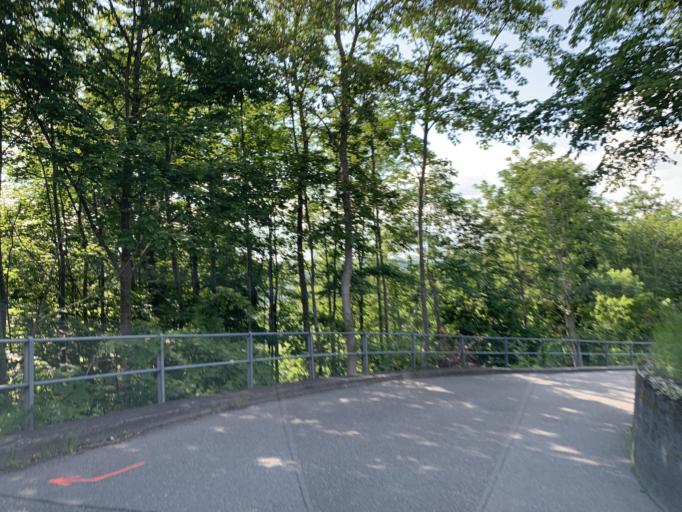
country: CH
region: Zurich
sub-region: Bezirk Winterthur
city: Seen (Kreis 3) / Waldegg
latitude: 47.4568
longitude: 8.7436
